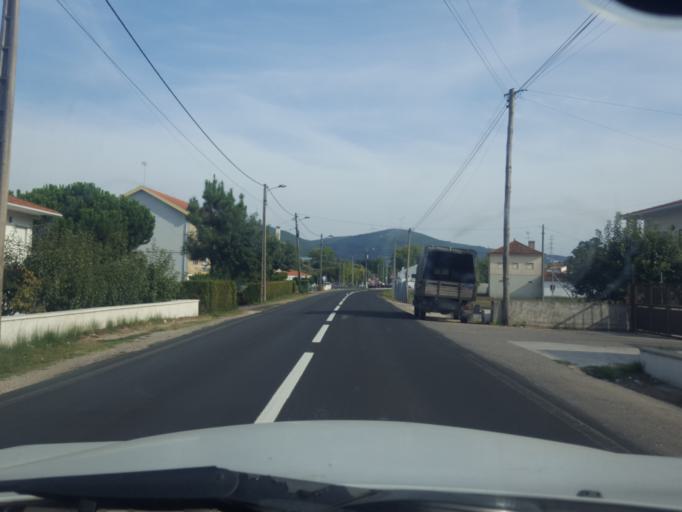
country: PT
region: Leiria
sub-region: Leiria
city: Leiria
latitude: 39.7016
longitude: -8.7906
